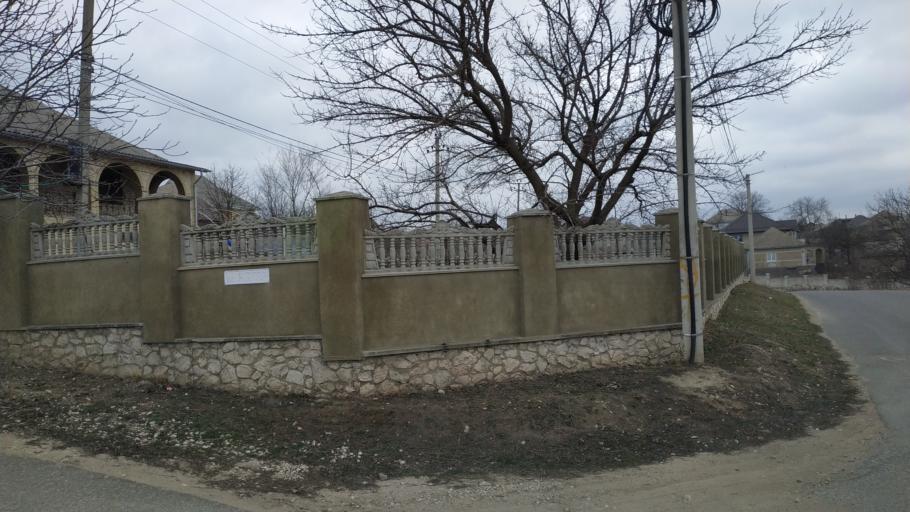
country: MD
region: Laloveni
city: Ialoveni
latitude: 46.9256
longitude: 28.7781
